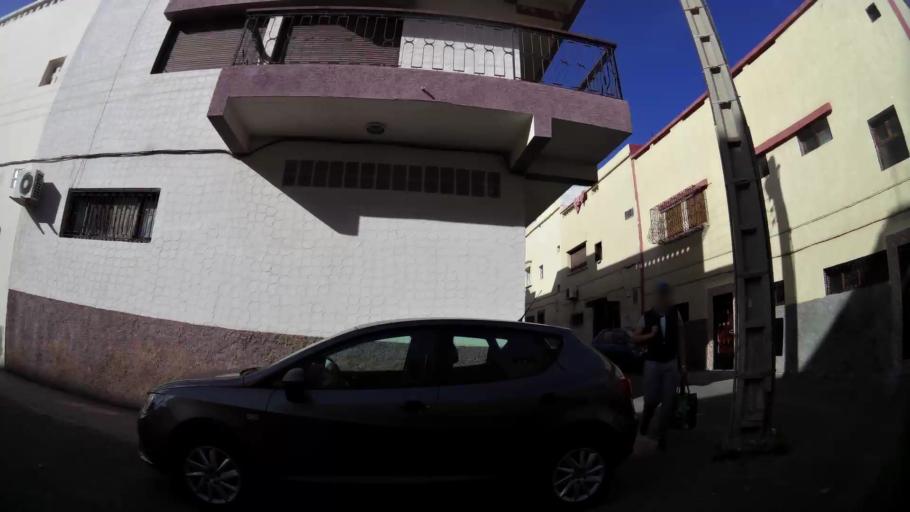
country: MA
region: Souss-Massa-Draa
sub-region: Agadir-Ida-ou-Tnan
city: Agadir
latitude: 30.4299
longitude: -9.5806
